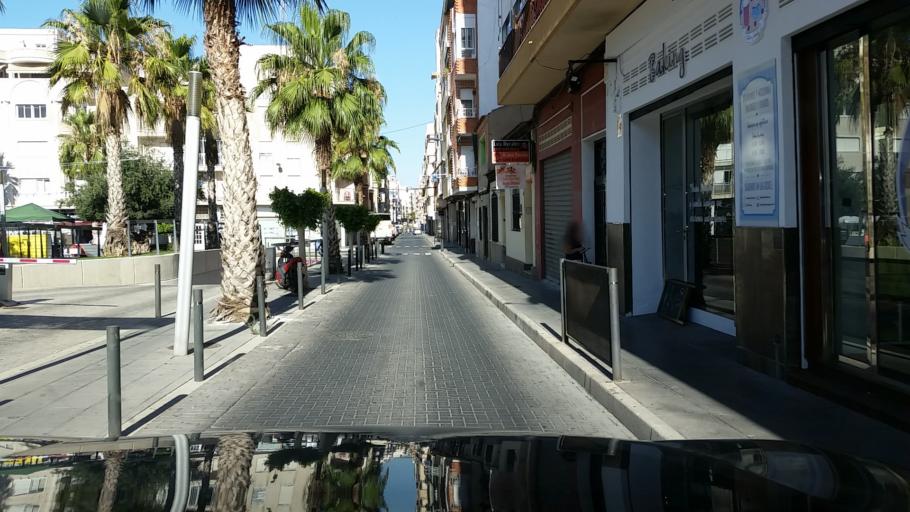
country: ES
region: Valencia
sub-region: Provincia de Alicante
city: Torrevieja
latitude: 37.9769
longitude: -0.6765
